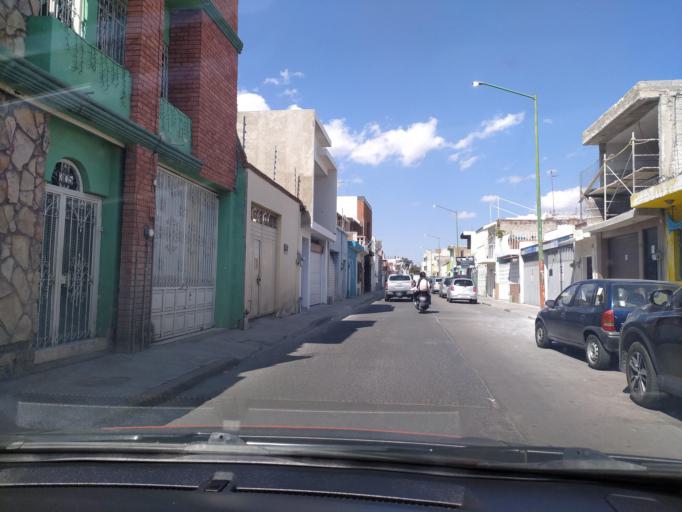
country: LA
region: Oudomxai
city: Muang La
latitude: 21.0235
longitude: 101.8569
